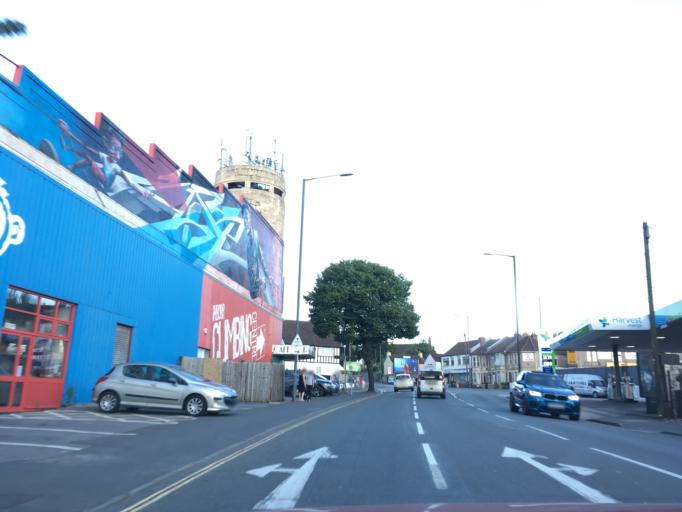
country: GB
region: England
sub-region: Bristol
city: Bristol
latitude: 51.4340
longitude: -2.6124
